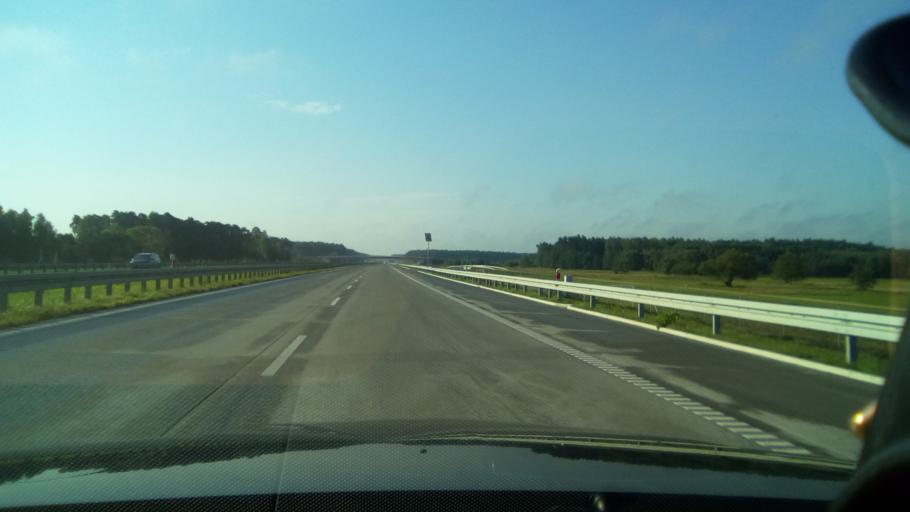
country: PL
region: Silesian Voivodeship
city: Wozniki
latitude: 50.5612
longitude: 19.0575
